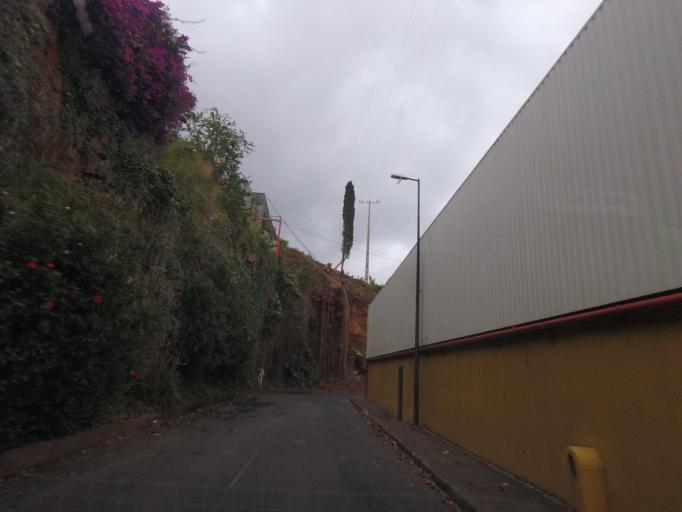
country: PT
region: Madeira
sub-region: Machico
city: Machico
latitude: 32.7023
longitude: -16.7750
